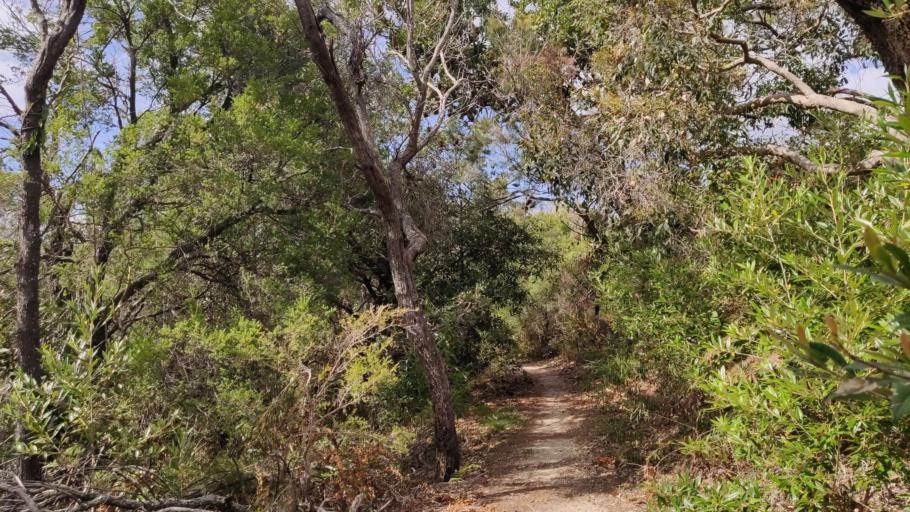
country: AU
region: New South Wales
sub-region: Port Macquarie-Hastings
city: North Haven
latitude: -31.6424
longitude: 152.8364
